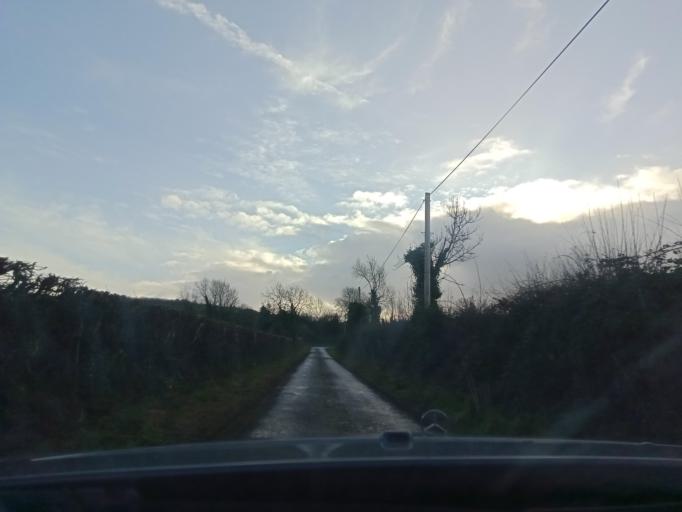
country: IE
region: Leinster
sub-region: Kilkenny
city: Callan
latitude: 52.4696
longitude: -7.3988
